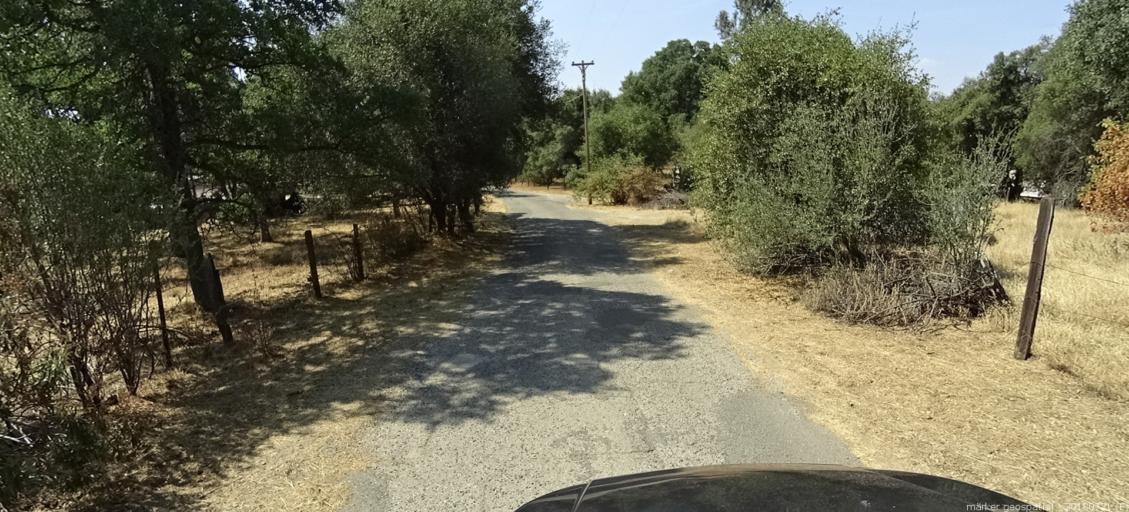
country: US
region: California
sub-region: Fresno County
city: Auberry
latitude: 37.2108
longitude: -119.5344
